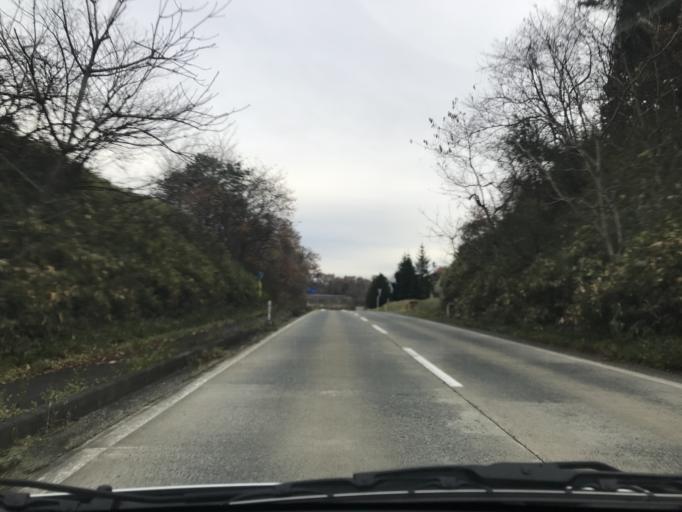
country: JP
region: Iwate
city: Kitakami
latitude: 39.2890
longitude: 141.2164
